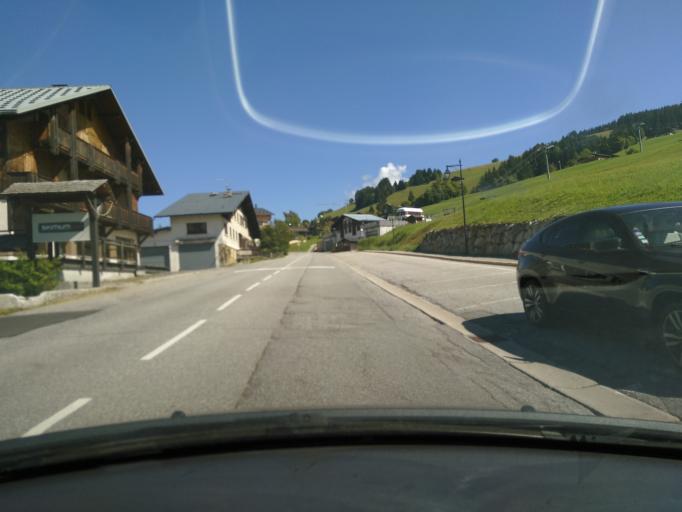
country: FR
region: Rhone-Alpes
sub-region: Departement de la Haute-Savoie
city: Praz-sur-Arly
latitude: 45.7954
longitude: 6.5066
